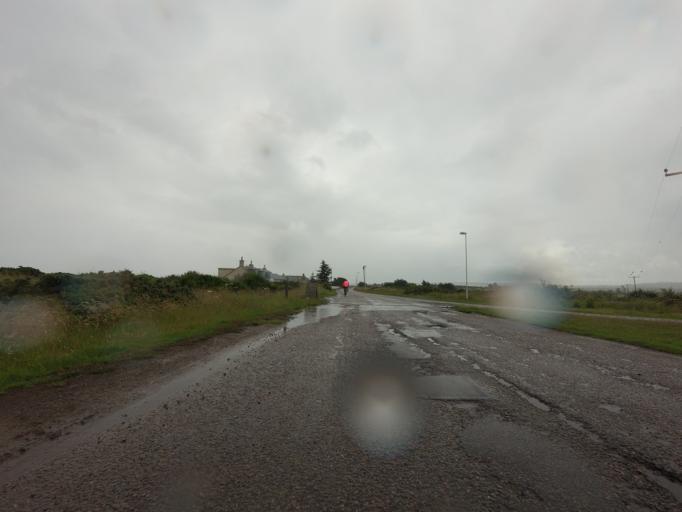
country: GB
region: Scotland
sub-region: Moray
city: Fochabers
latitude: 57.6732
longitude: -3.0900
